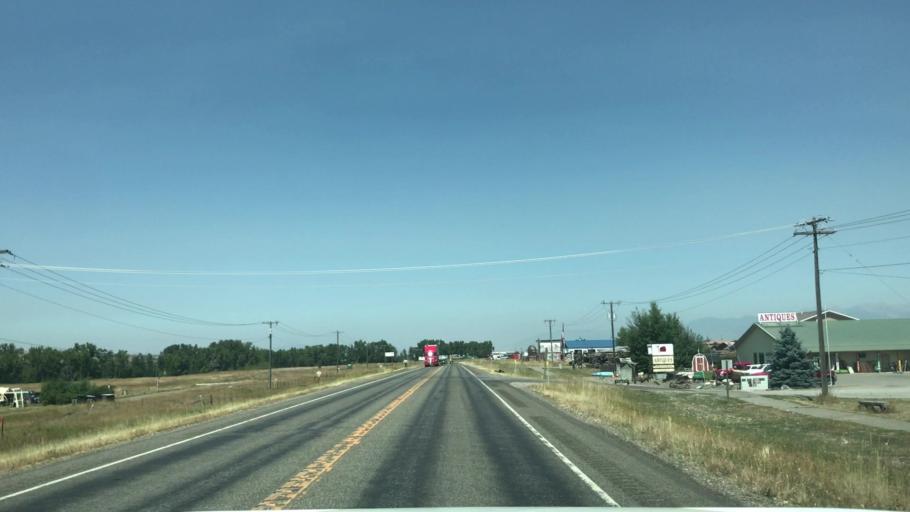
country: US
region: Montana
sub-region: Gallatin County
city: Four Corners
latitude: 45.6022
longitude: -111.1962
